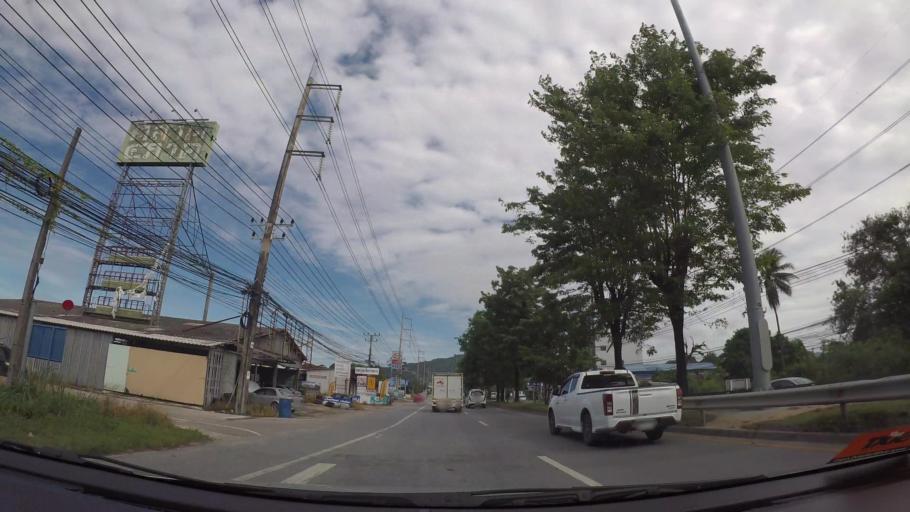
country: TH
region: Rayong
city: Ban Chang
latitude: 12.7409
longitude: 101.1210
